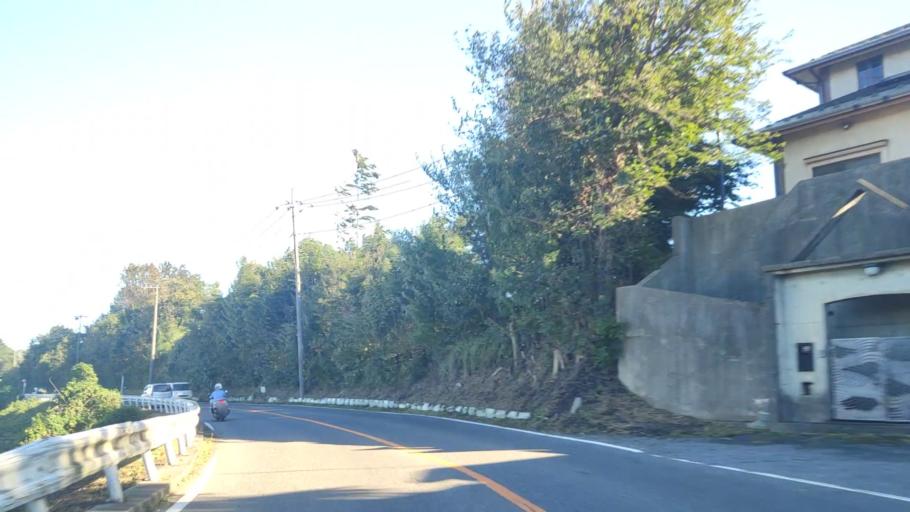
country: JP
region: Kanagawa
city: Zama
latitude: 35.5190
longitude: 139.3624
